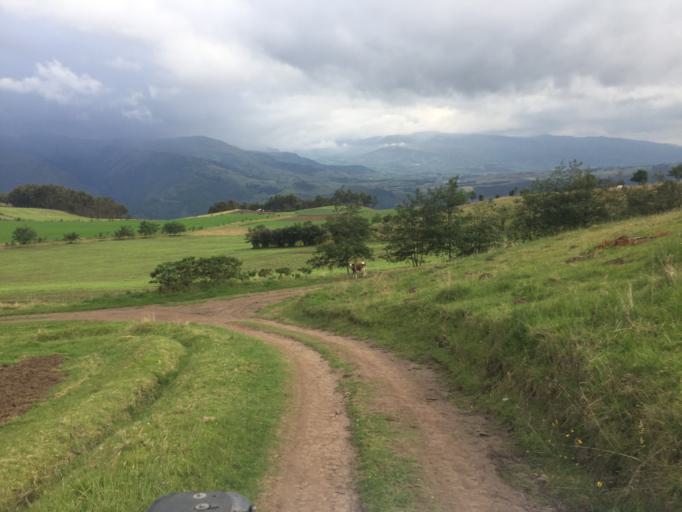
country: EC
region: Imbabura
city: Ibarra
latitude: 0.2261
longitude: -78.1202
